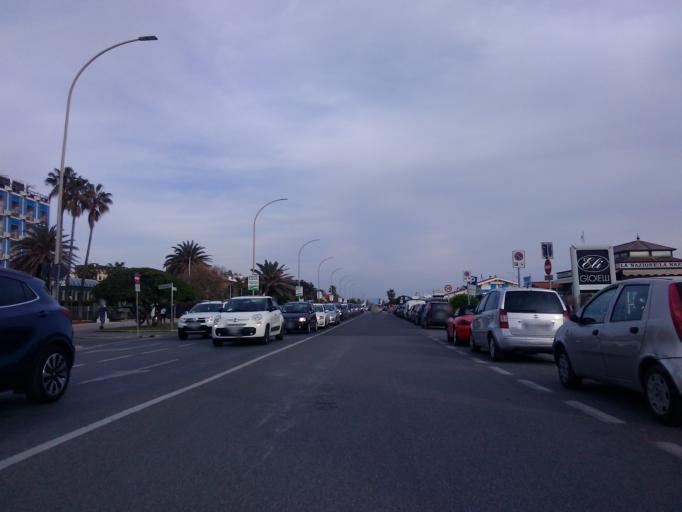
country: IT
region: Tuscany
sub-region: Provincia di Massa-Carrara
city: Massa
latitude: 44.0076
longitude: 10.0994
